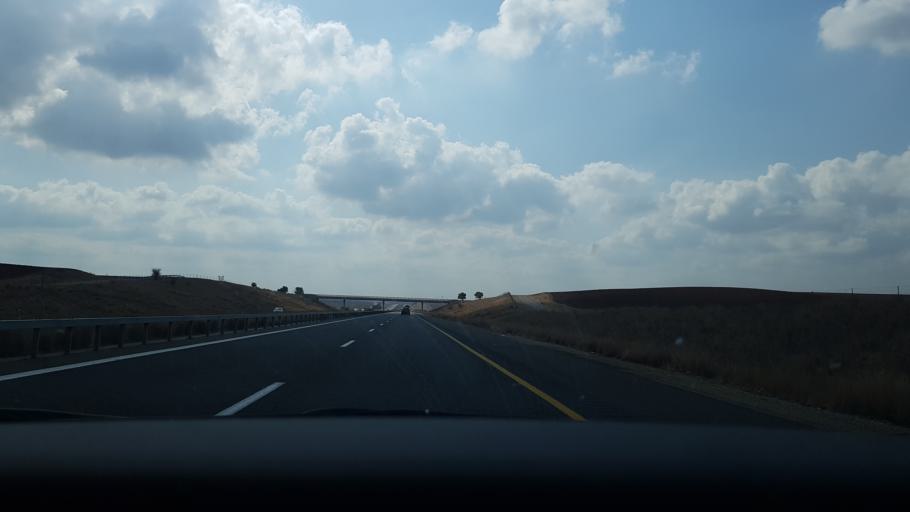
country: IL
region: Southern District
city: Qiryat Gat
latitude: 31.6625
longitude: 34.8079
